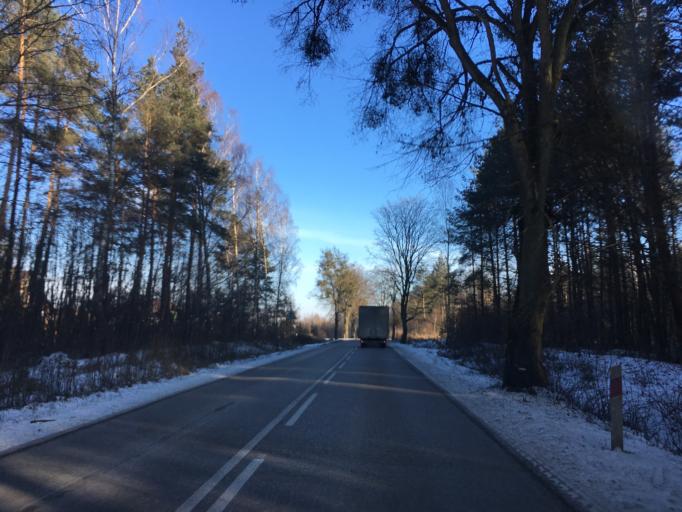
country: PL
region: Pomeranian Voivodeship
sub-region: Powiat starogardzki
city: Zblewo
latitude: 53.9481
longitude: 18.3035
